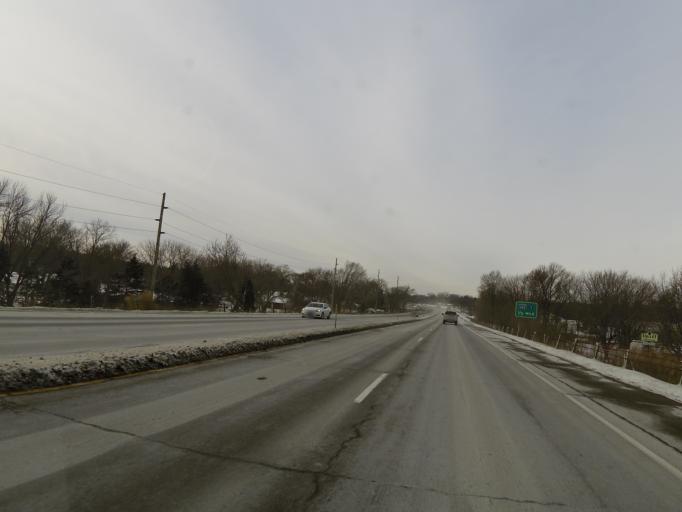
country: US
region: Minnesota
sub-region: Scott County
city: Jordan
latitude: 44.6733
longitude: -93.6297
